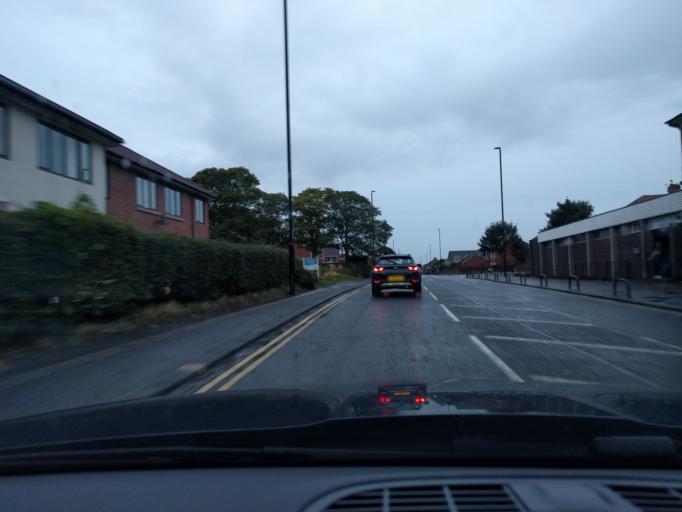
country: GB
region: England
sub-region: Northumberland
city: Backworth
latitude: 55.0262
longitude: -1.5575
